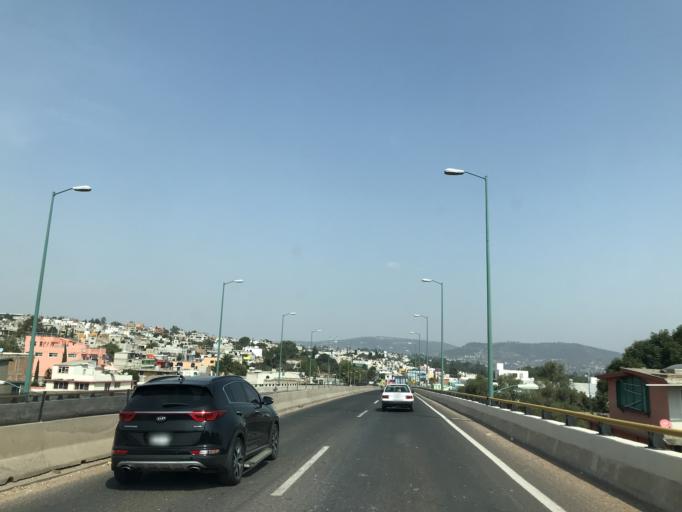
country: MX
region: Tlaxcala
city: Tlaxcala de Xicohtencatl
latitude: 19.3120
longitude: -98.2018
